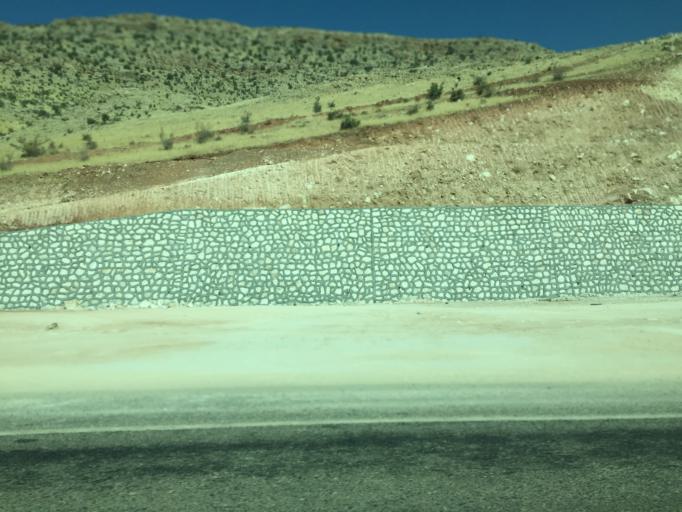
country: TR
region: Batman
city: Hasankeyf
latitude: 37.6917
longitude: 41.4570
